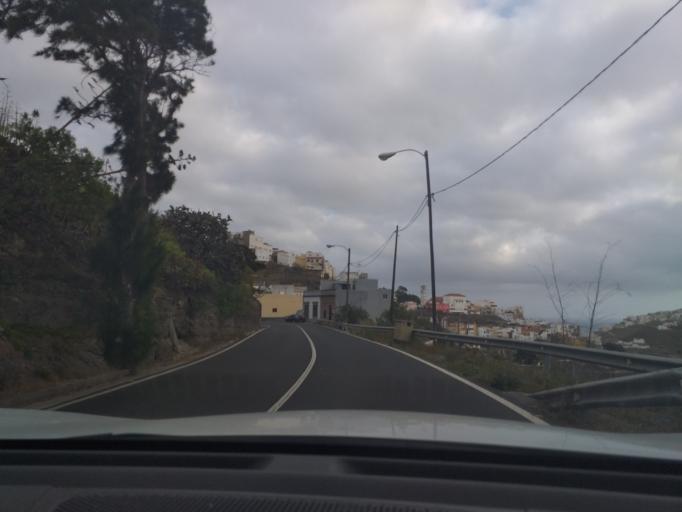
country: ES
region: Canary Islands
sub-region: Provincia de Las Palmas
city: Arucas
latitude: 28.1130
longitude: -15.4922
